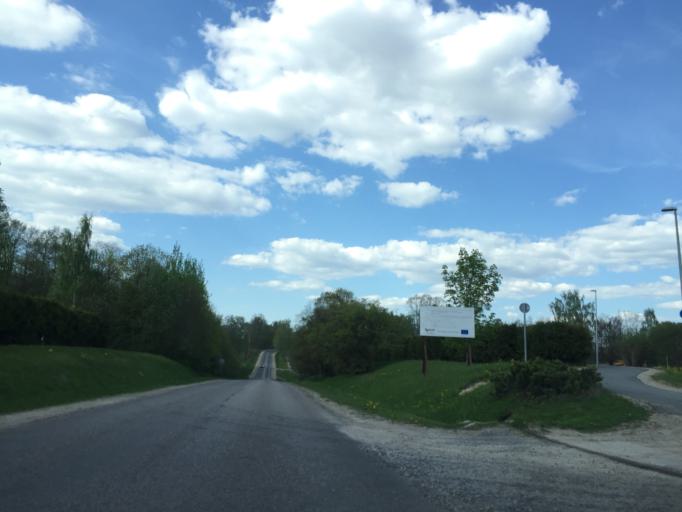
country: LV
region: Limbazu Rajons
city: Limbazi
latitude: 57.4870
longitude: 24.7100
